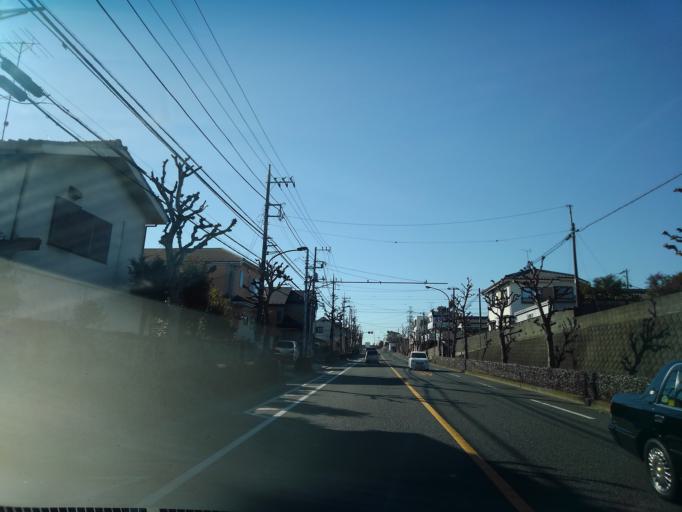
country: JP
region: Tokyo
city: Hino
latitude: 35.6785
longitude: 139.3658
